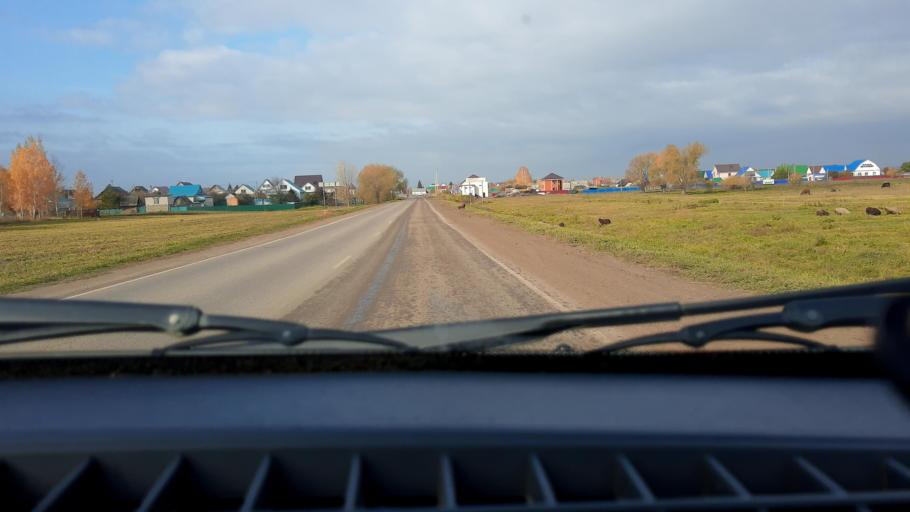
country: RU
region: Bashkortostan
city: Kabakovo
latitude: 54.5482
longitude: 56.1026
